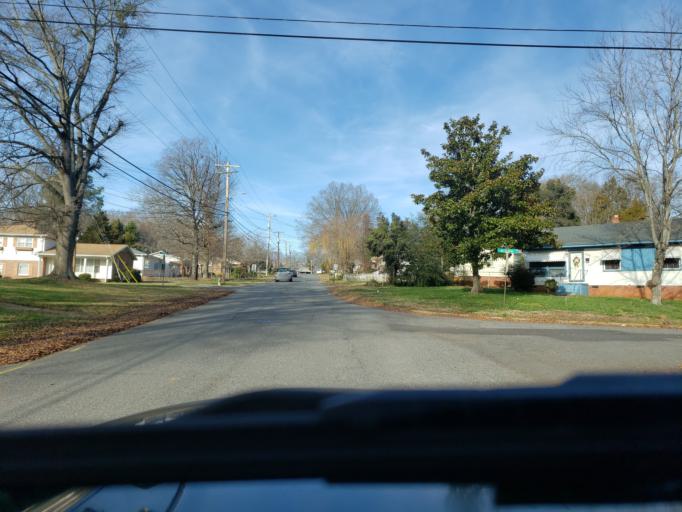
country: US
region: North Carolina
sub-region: Cleveland County
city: Kings Mountain
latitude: 35.2467
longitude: -81.3508
